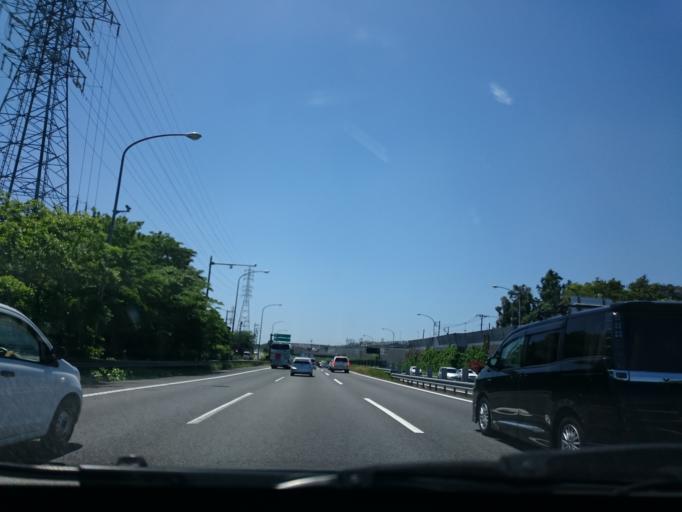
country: JP
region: Kanagawa
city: Minami-rinkan
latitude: 35.5023
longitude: 139.4788
